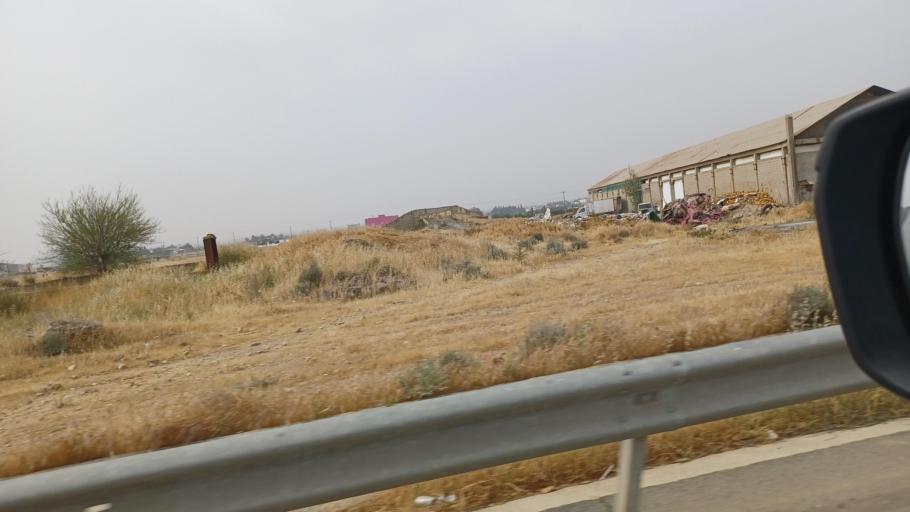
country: CY
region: Lefkosia
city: Kokkinotrimithia
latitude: 35.1589
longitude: 33.2178
